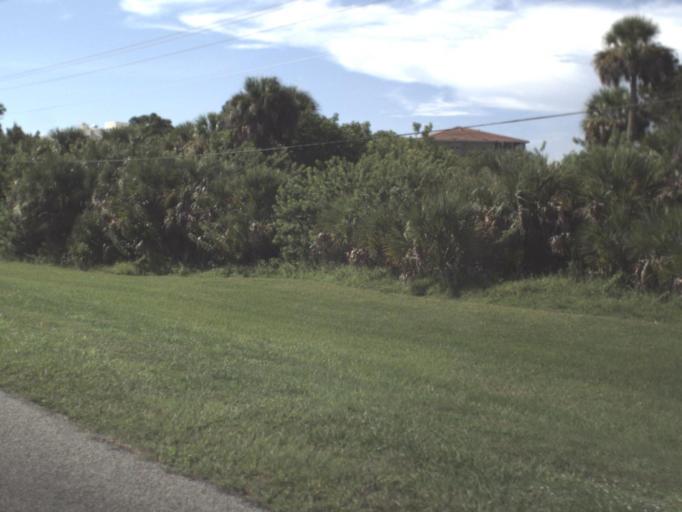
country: US
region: Florida
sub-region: Sarasota County
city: Laurel
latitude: 27.1677
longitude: -82.4770
